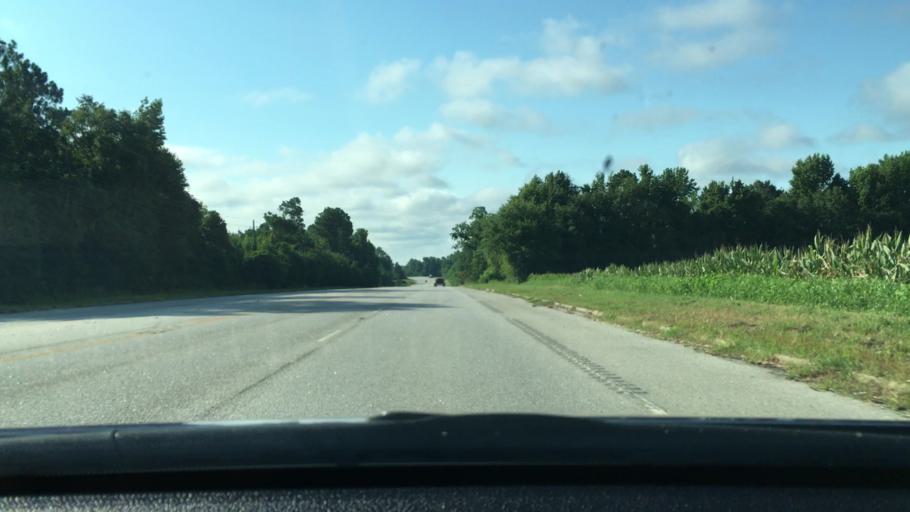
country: US
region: South Carolina
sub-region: Clarendon County
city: Manning
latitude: 33.7557
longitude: -80.2248
